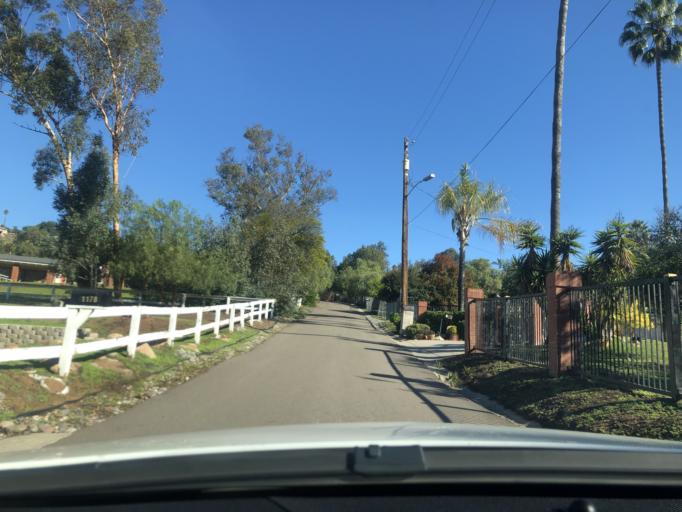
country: US
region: California
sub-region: San Diego County
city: El Cajon
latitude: 32.7777
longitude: -116.9405
